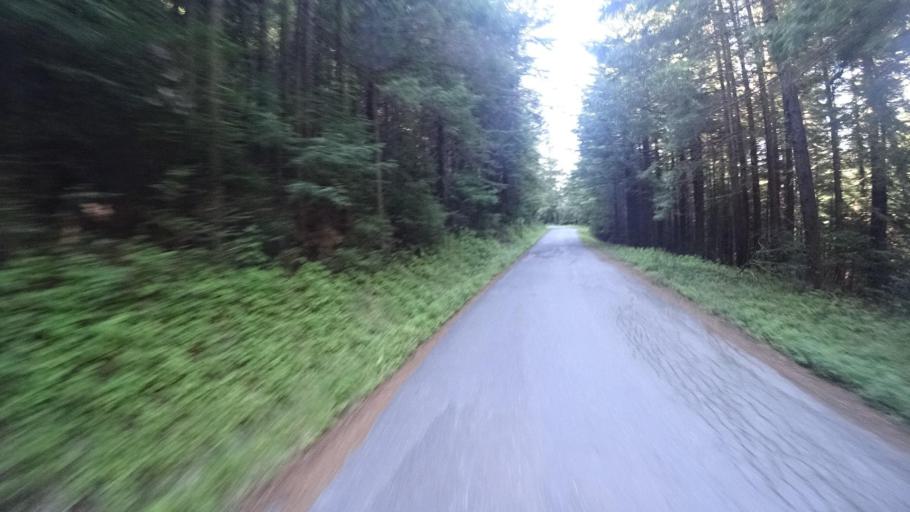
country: US
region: California
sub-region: Humboldt County
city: Rio Dell
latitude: 40.4601
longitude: -123.9948
